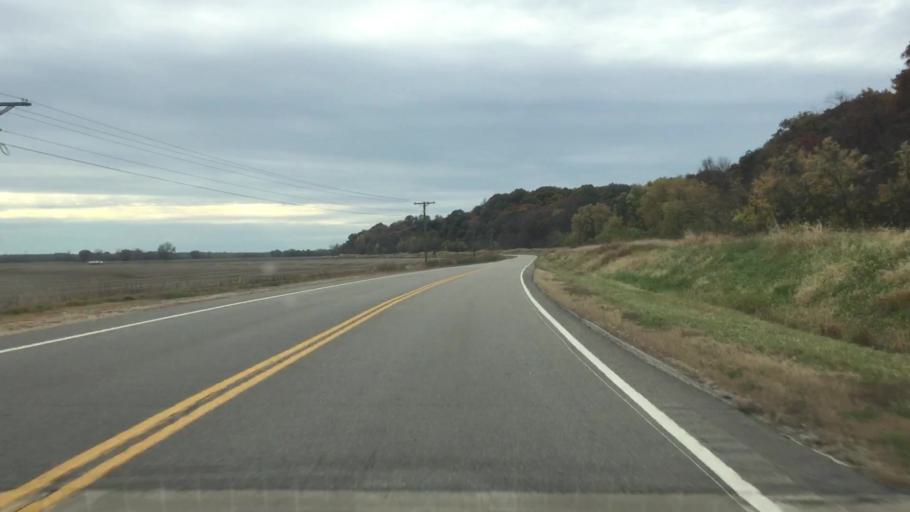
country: US
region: Missouri
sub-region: Callaway County
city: Holts Summit
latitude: 38.5871
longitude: -92.0337
